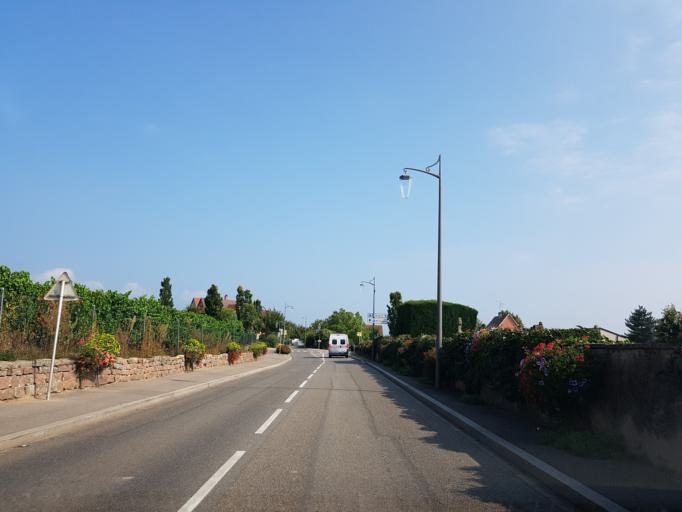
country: FR
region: Alsace
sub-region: Departement du Haut-Rhin
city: Eguisheim
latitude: 48.0427
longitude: 7.3118
